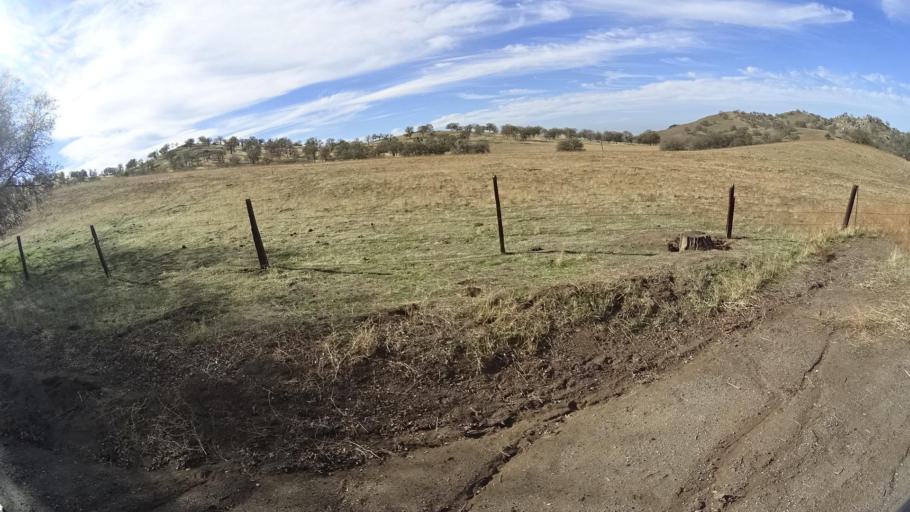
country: US
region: California
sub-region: Kern County
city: Oildale
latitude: 35.5762
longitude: -118.8111
